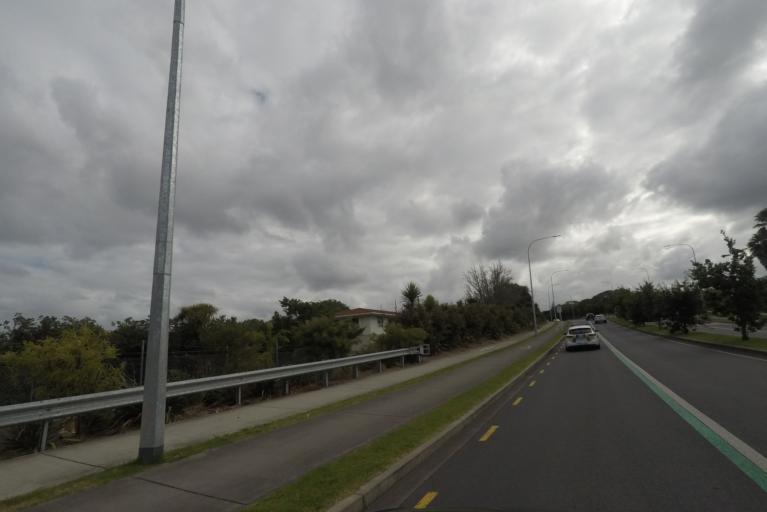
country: NZ
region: Auckland
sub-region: Auckland
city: Rothesay Bay
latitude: -36.7322
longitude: 174.6940
